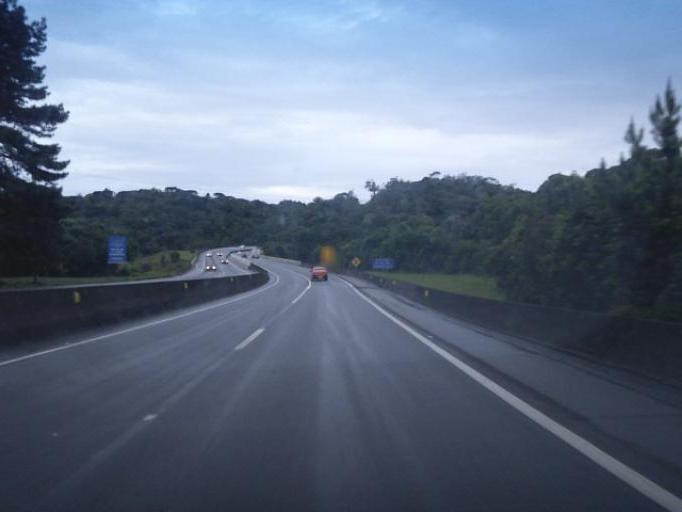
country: BR
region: Parana
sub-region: Sao Jose Dos Pinhais
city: Sao Jose dos Pinhais
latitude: -25.8452
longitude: -49.0771
